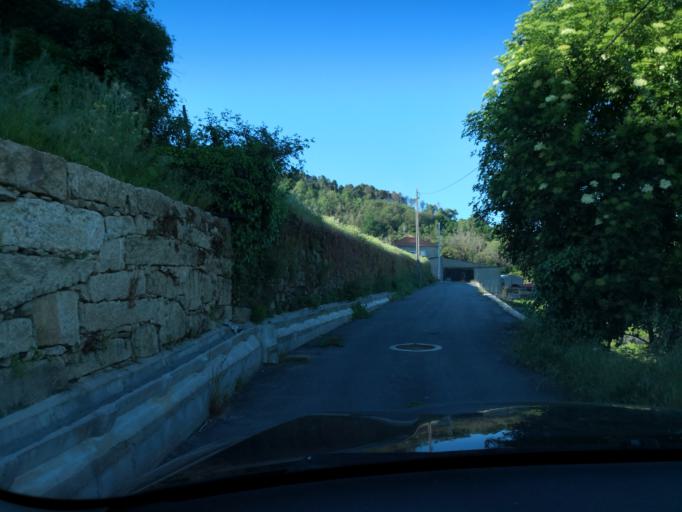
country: PT
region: Vila Real
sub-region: Vila Real
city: Vila Real
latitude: 41.3303
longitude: -7.7468
